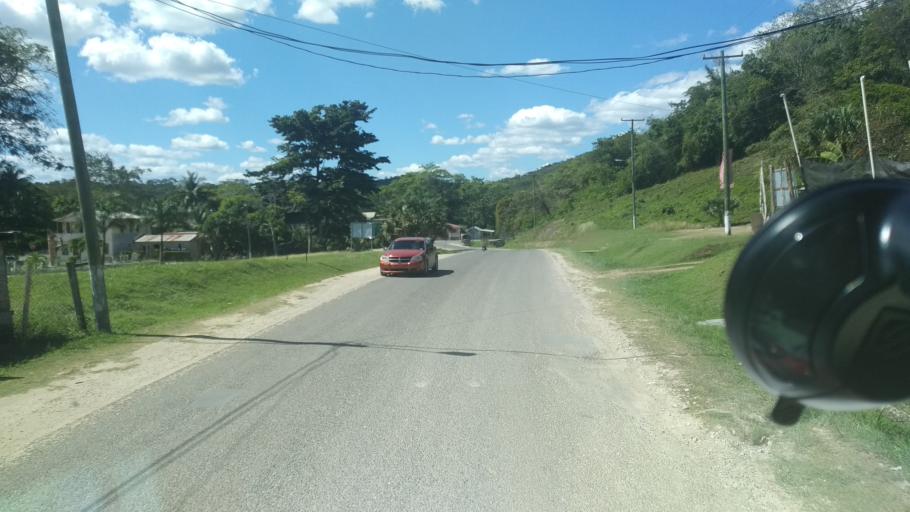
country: BZ
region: Cayo
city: Benque Viejo del Carmen
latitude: 17.0773
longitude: -89.1354
